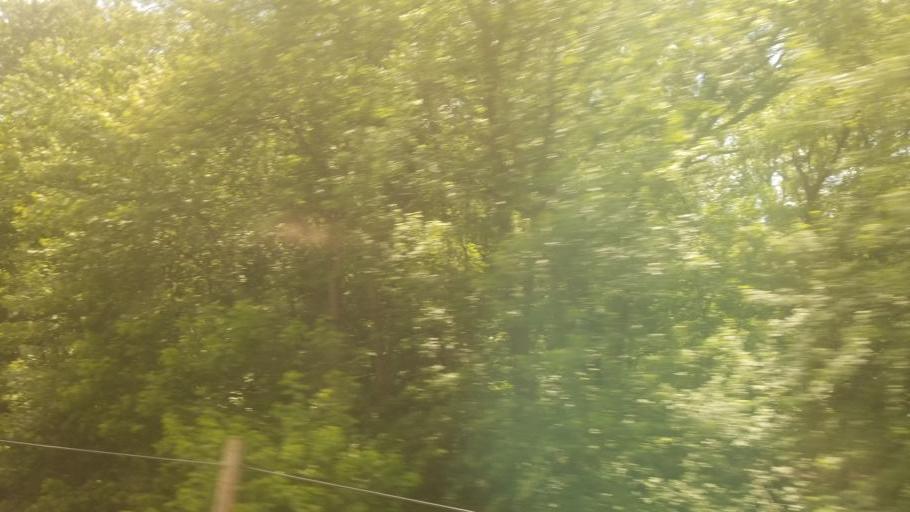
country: US
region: Maryland
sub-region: Frederick County
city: Brunswick
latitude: 39.3164
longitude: -77.6482
